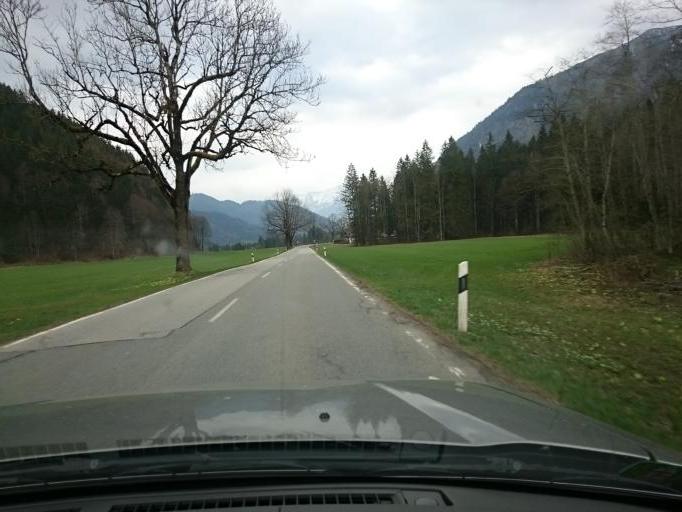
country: DE
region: Bavaria
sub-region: Upper Bavaria
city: Oberammergau
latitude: 47.5747
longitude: 11.0399
